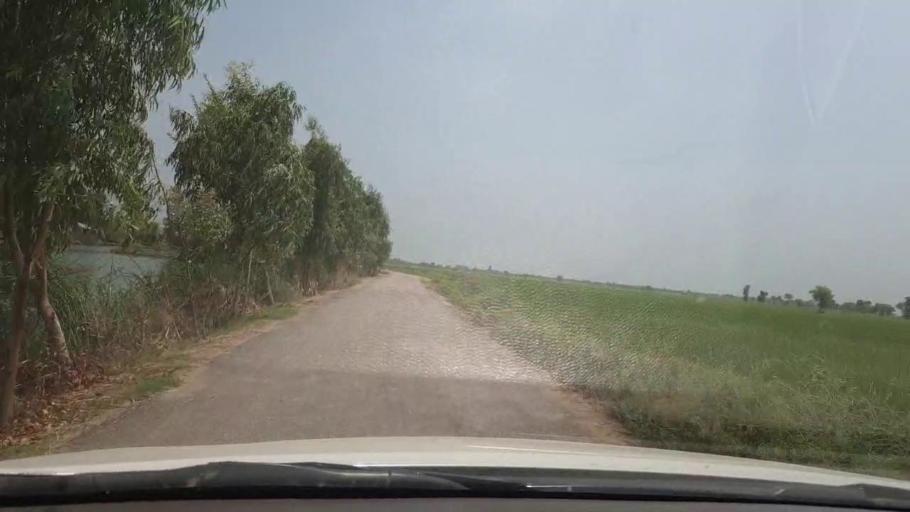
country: PK
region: Sindh
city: Shikarpur
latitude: 28.0927
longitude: 68.6257
